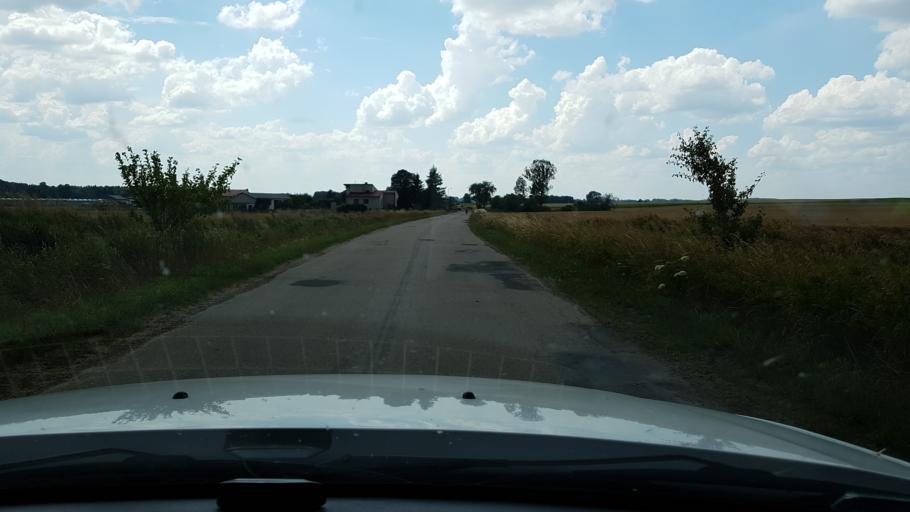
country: PL
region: Greater Poland Voivodeship
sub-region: Powiat pilski
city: Szydlowo
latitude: 53.2027
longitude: 16.5531
